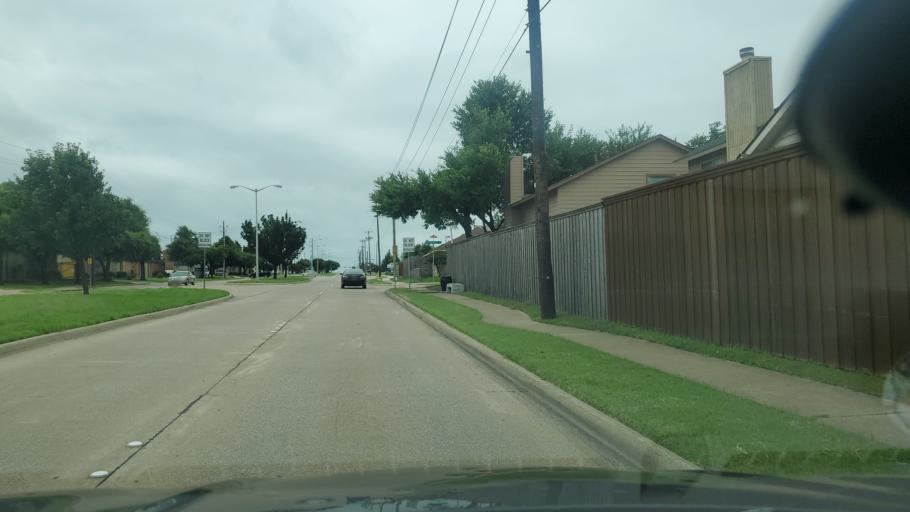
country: US
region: Texas
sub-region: Dallas County
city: Garland
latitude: 32.9489
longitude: -96.6654
